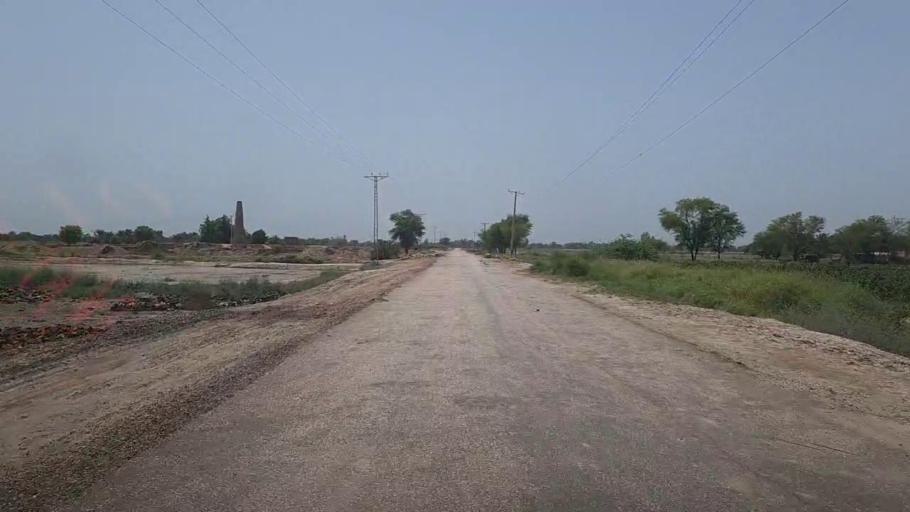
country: PK
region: Sindh
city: Pad Idan
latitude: 26.8343
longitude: 68.3167
